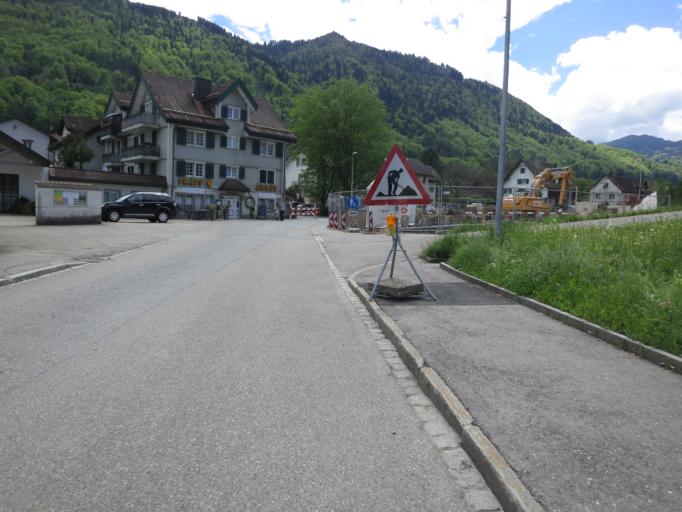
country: CH
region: Schwyz
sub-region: Bezirk March
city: Schubelbach
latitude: 47.1732
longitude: 8.9277
